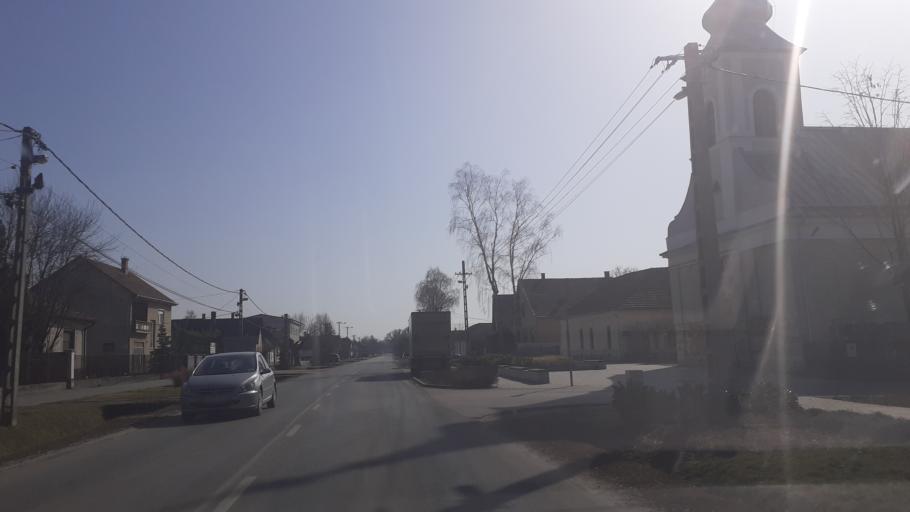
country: HU
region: Pest
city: Dabas
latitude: 47.1721
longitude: 19.3219
